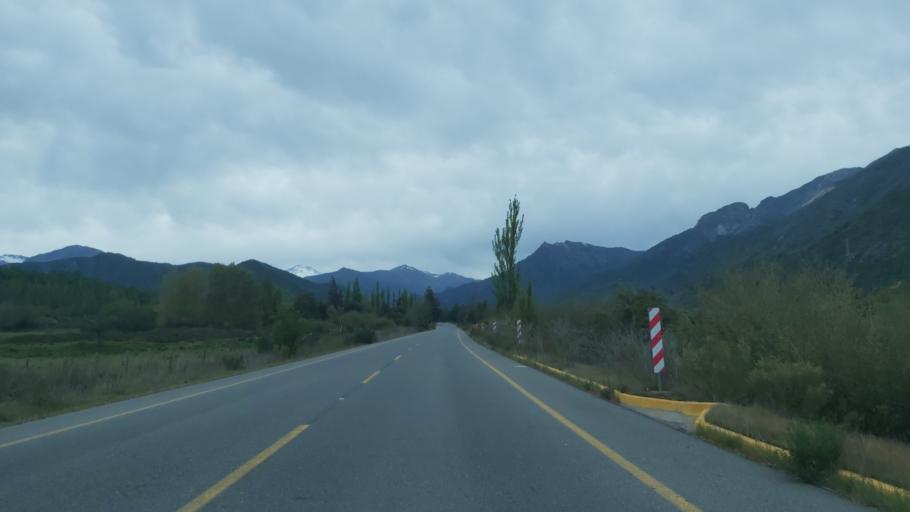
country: CL
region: Maule
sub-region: Provincia de Linares
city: Colbun
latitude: -35.7435
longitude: -71.0080
